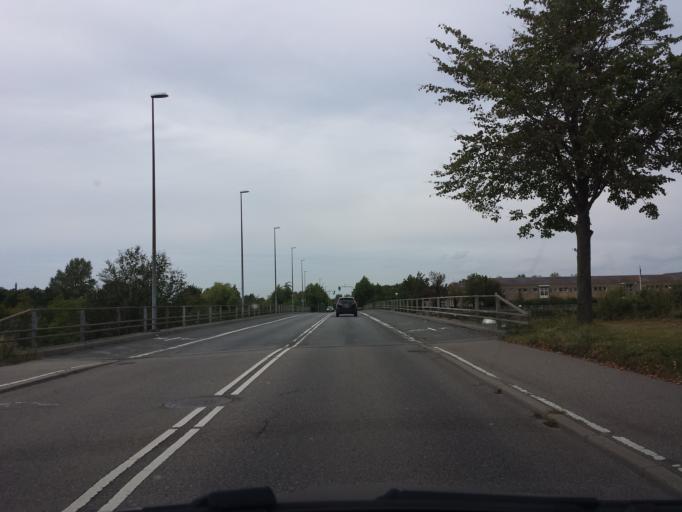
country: DK
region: Capital Region
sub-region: Hoje-Taastrup Kommune
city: Taastrup
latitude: 55.6477
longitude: 12.2661
